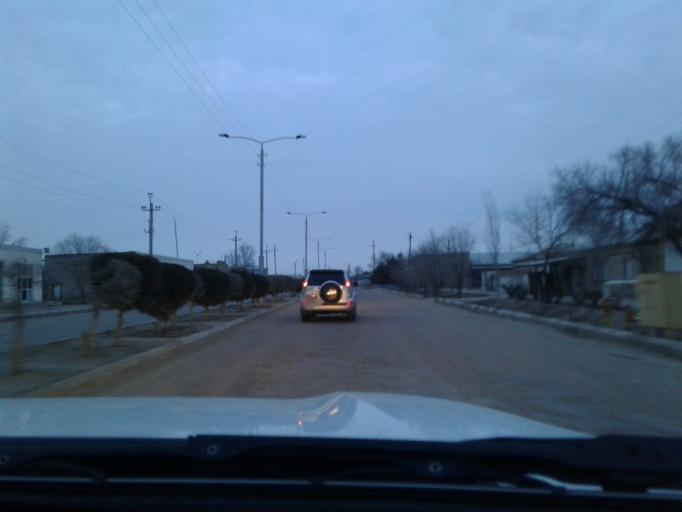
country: UZ
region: Karakalpakstan
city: Manghit
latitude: 42.0718
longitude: 59.9468
